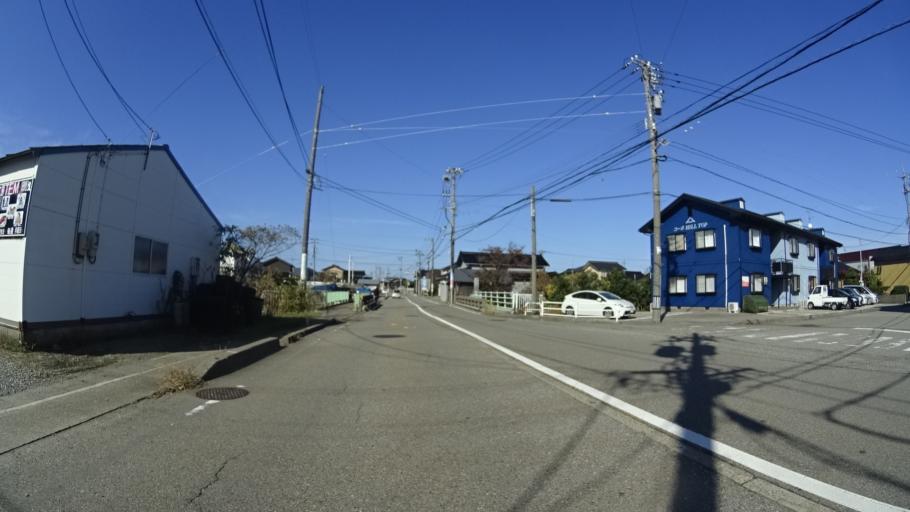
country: JP
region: Ishikawa
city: Kanazawa-shi
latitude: 36.6059
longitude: 136.6068
